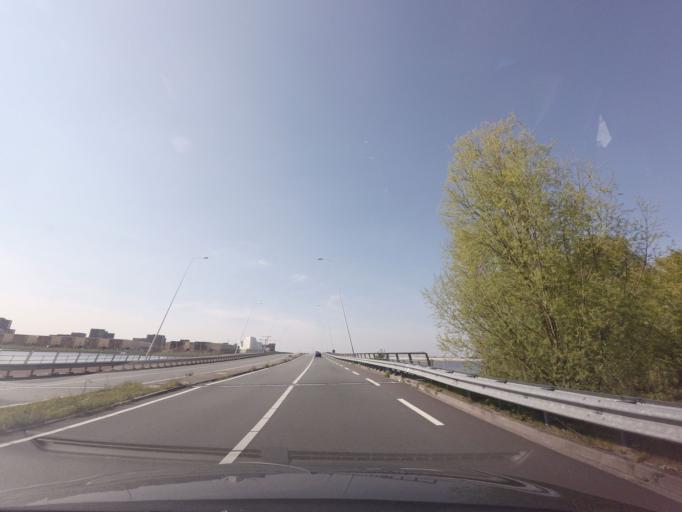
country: NL
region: North Holland
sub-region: Gemeente Amsterdam
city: Driemond
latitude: 52.3456
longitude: 5.0162
